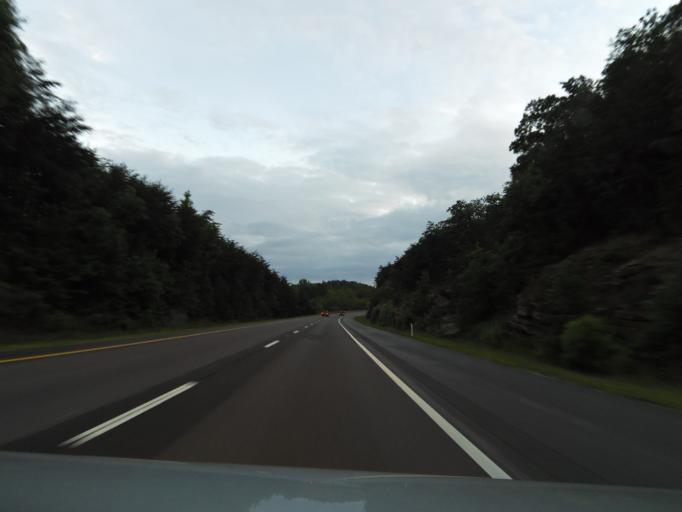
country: US
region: Tennessee
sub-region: Campbell County
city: LaFollette
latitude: 36.4767
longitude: -84.2242
